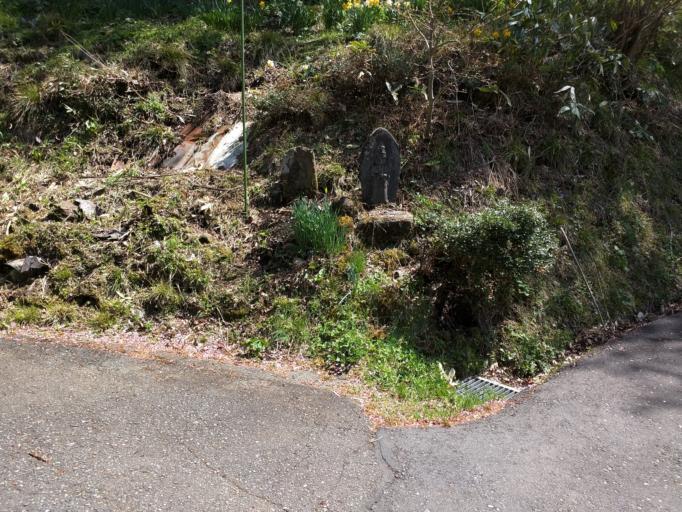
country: JP
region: Nagano
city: Nagano-shi
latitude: 36.7391
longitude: 138.0845
